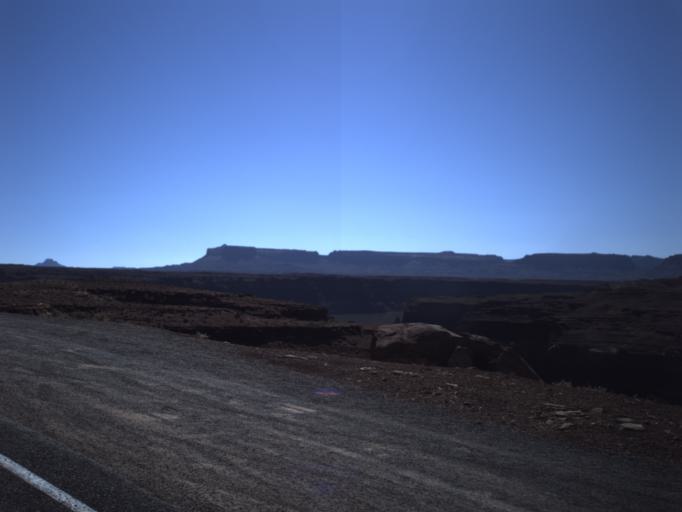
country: US
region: Utah
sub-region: San Juan County
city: Blanding
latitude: 37.8821
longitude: -110.4226
